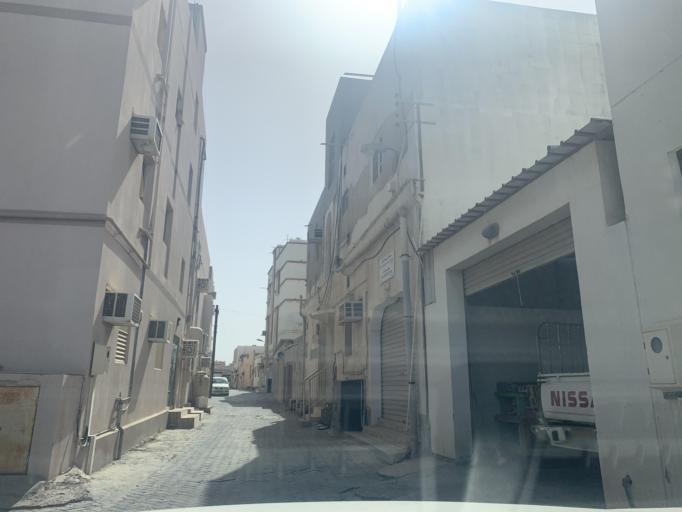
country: BH
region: Northern
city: Sitrah
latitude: 26.1690
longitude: 50.6265
